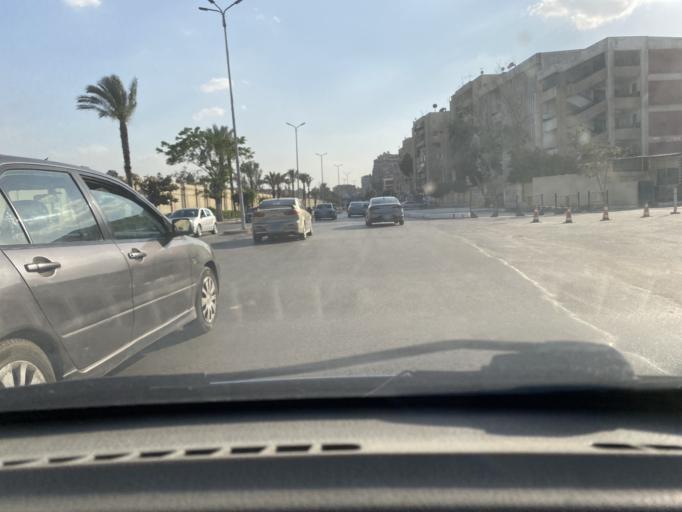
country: EG
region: Muhafazat al Qahirah
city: Cairo
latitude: 30.0940
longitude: 31.2952
